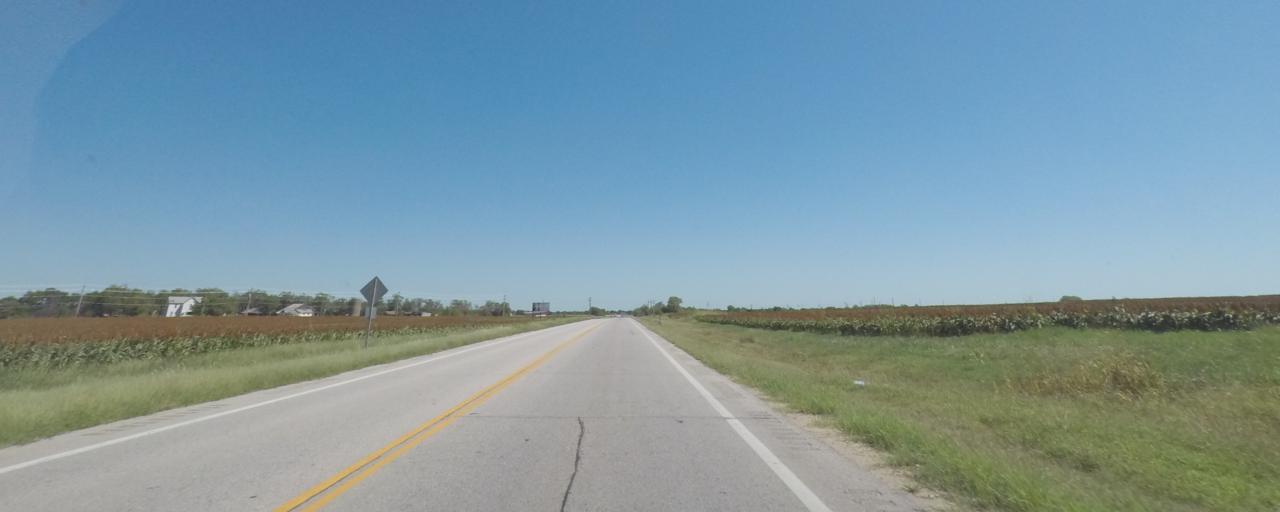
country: US
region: Kansas
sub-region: Sumner County
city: Wellington
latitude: 37.3013
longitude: -97.3929
